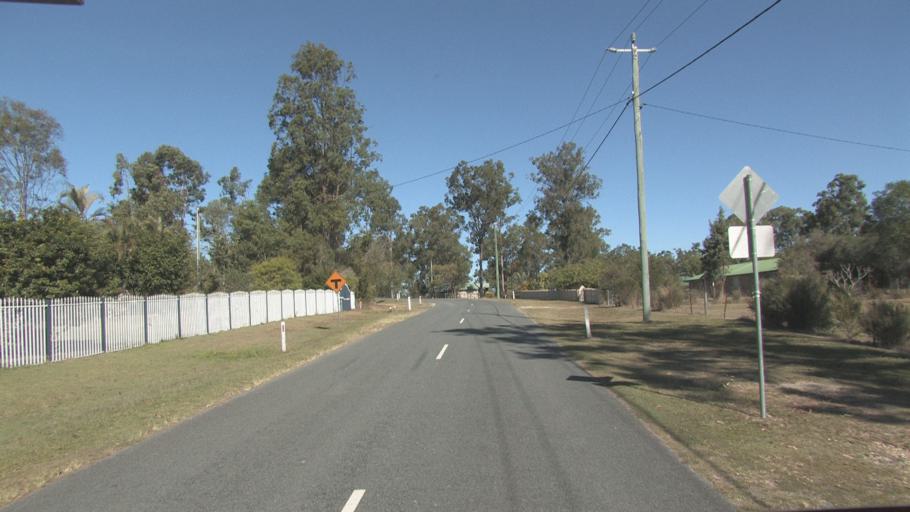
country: AU
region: Queensland
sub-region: Logan
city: North Maclean
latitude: -27.7295
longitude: 152.9615
